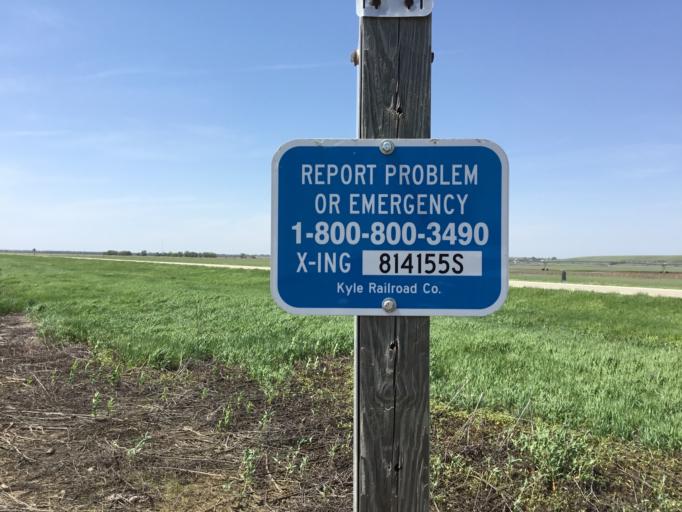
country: US
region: Kansas
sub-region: Mitchell County
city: Beloit
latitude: 39.4225
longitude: -98.0162
